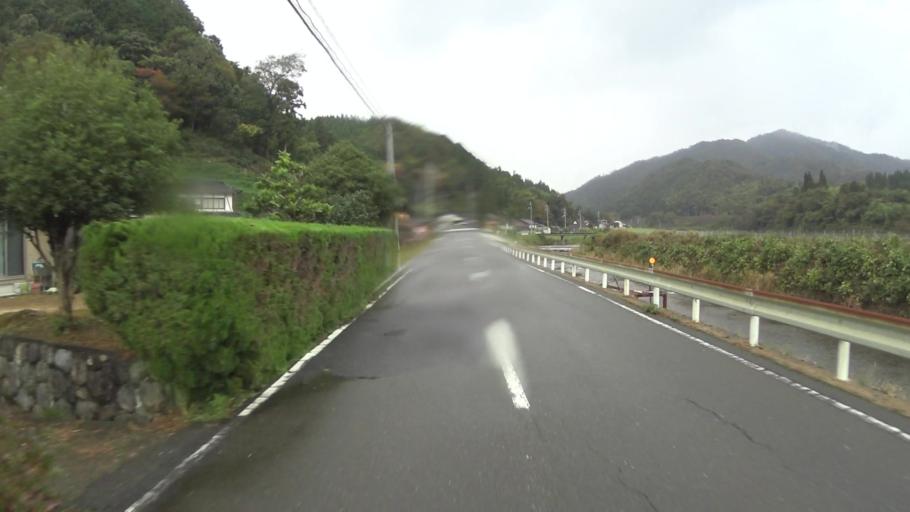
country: JP
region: Kyoto
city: Miyazu
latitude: 35.4167
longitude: 135.1542
